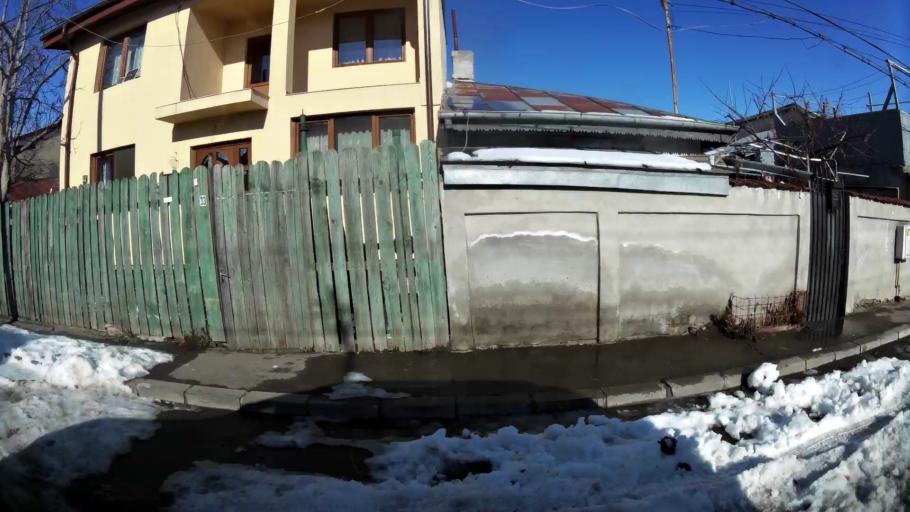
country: RO
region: Ilfov
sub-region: Comuna Magurele
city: Magurele
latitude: 44.3985
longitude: 26.0517
